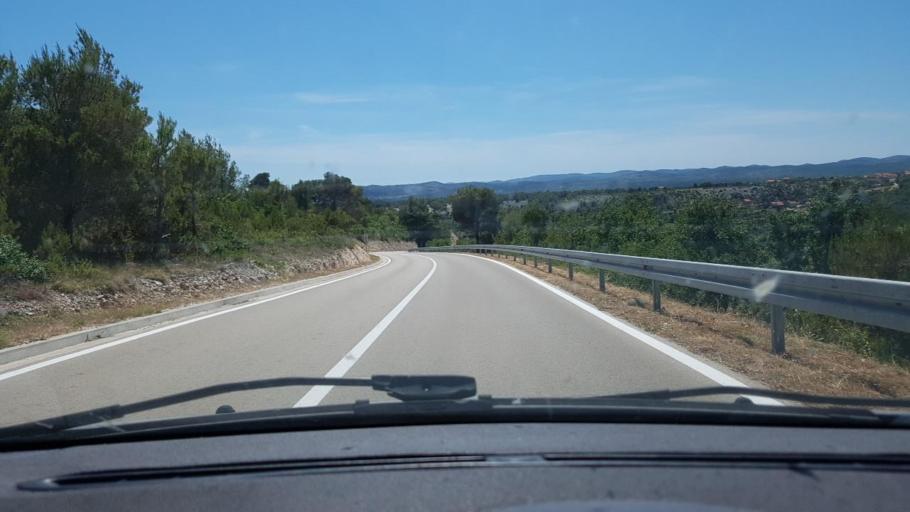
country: HR
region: Sibensko-Kniniska
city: Zaton
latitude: 43.8501
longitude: 15.9056
